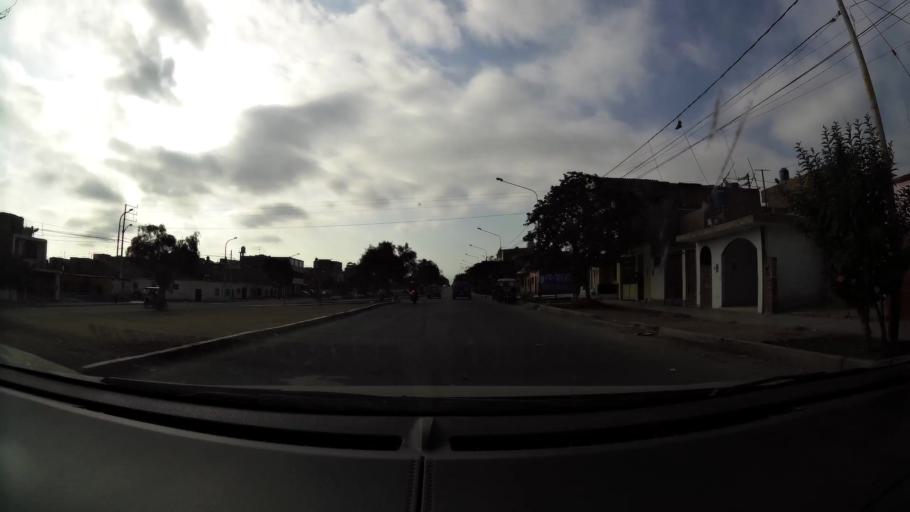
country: PE
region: La Libertad
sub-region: Provincia de Trujillo
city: La Esperanza
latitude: -8.0810
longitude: -79.0425
